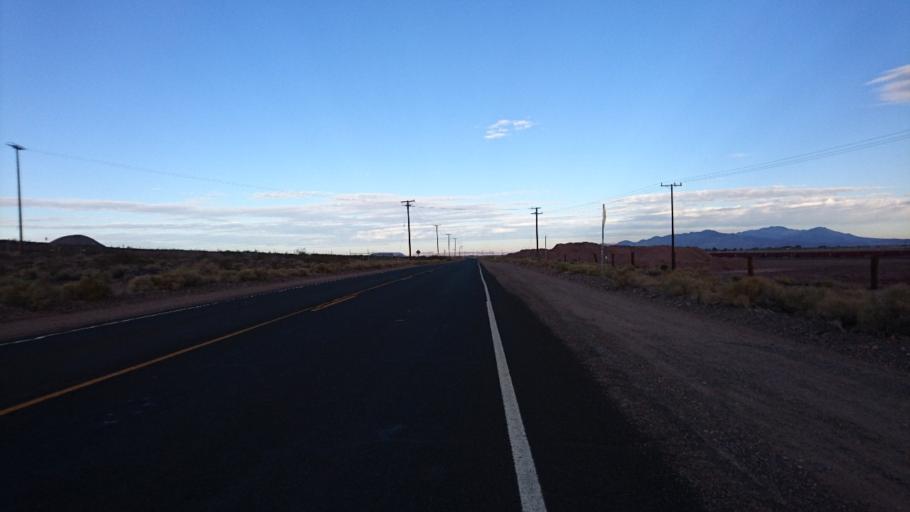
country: US
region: California
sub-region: San Bernardino County
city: Barstow
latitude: 34.8317
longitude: -116.6969
